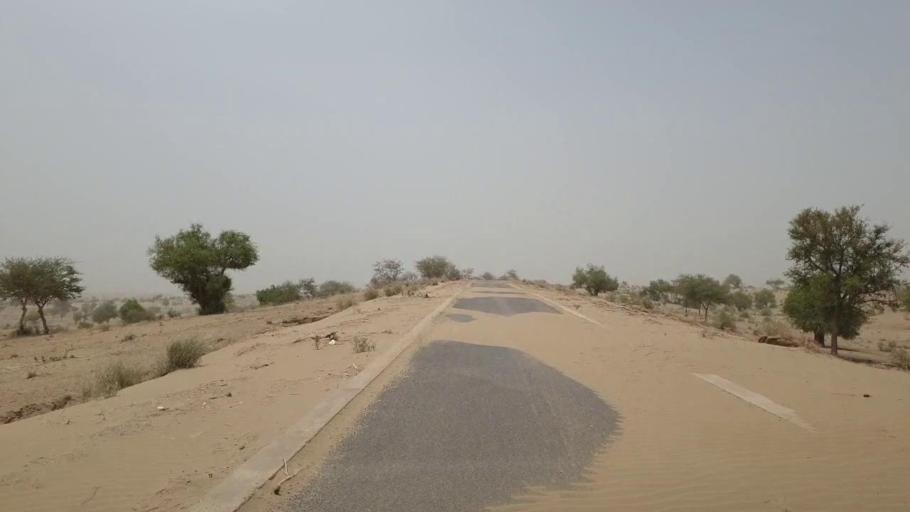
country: PK
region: Sindh
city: Islamkot
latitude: 24.7994
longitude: 70.5189
